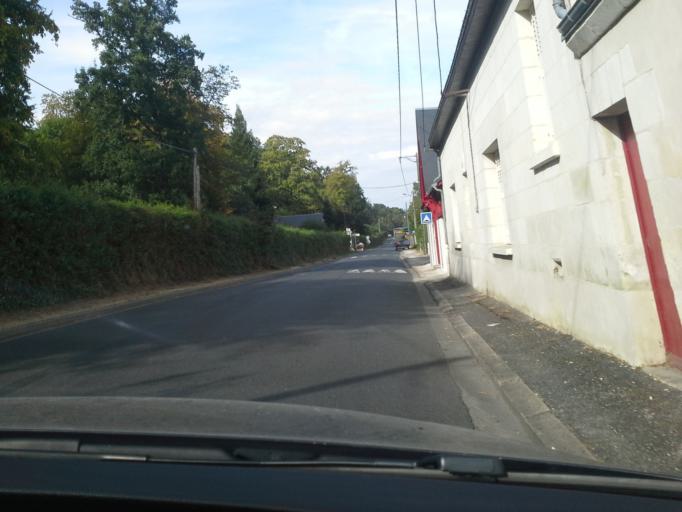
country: FR
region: Centre
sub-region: Departement d'Indre-et-Loire
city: Reugny
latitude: 47.4841
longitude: 0.8857
